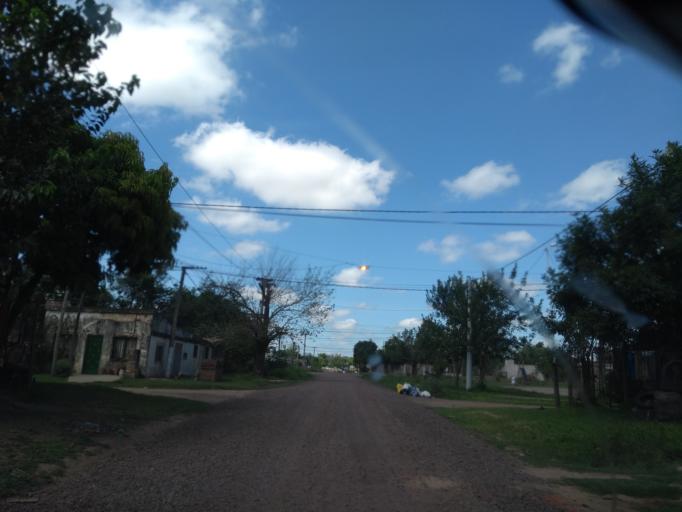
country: AR
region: Chaco
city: Fontana
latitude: -27.4072
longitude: -59.0421
